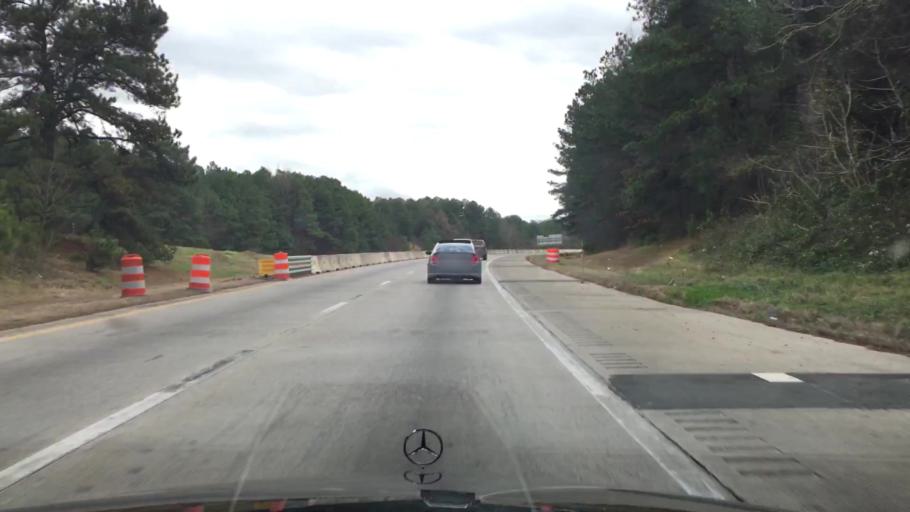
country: US
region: North Carolina
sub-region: Wake County
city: Garner
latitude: 35.7524
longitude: -78.5964
